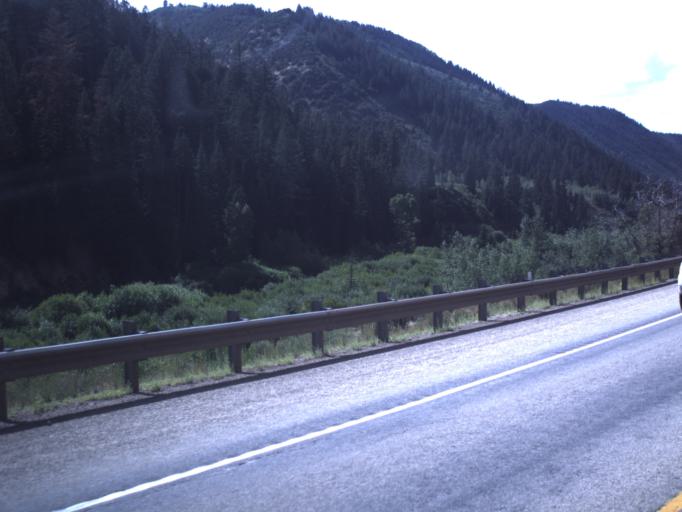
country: US
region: Utah
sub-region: Wasatch County
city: Heber
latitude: 40.3444
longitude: -111.2653
